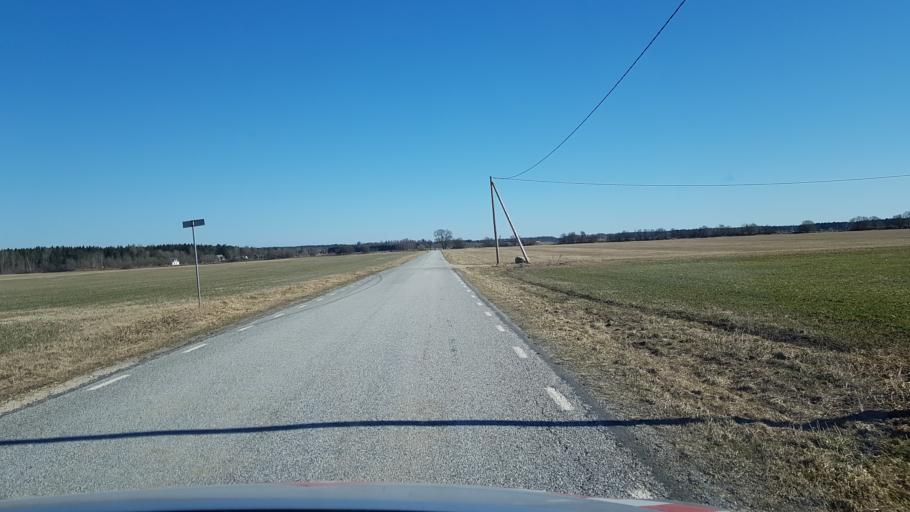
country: EE
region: Laeaene-Virumaa
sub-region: Viru-Nigula vald
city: Kunda
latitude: 59.4060
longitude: 26.5377
